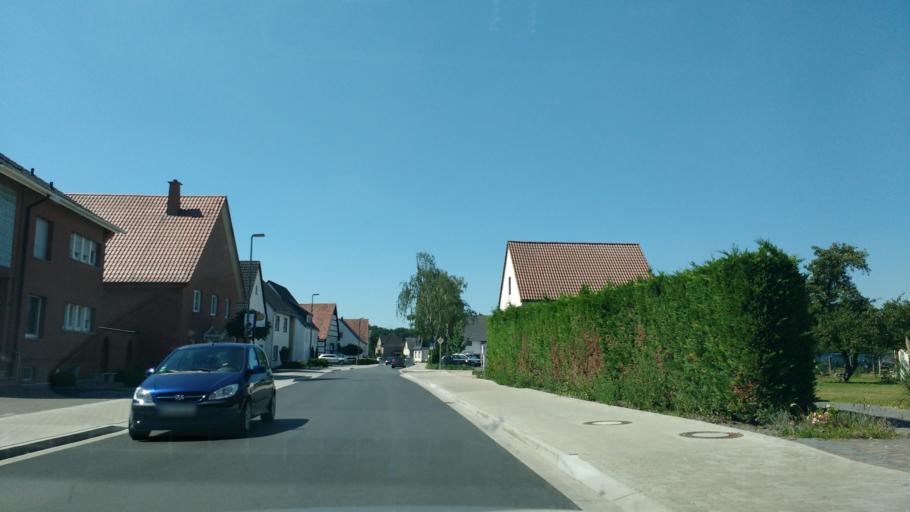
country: DE
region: North Rhine-Westphalia
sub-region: Regierungsbezirk Arnsberg
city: Lippstadt
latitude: 51.6895
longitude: 8.3714
